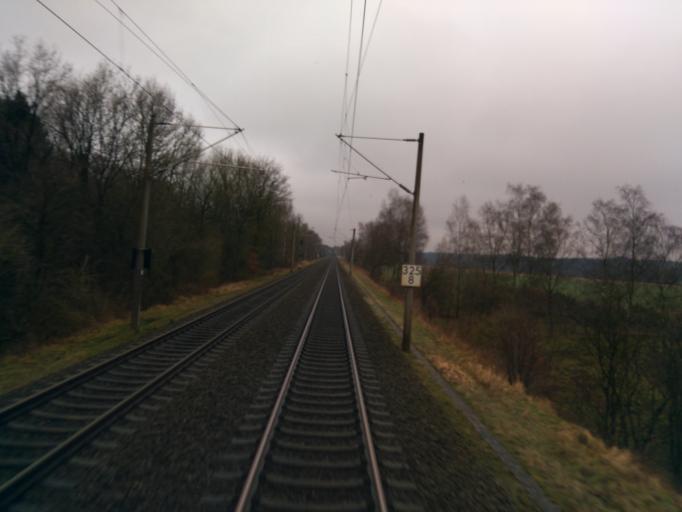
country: DE
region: Lower Saxony
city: Buchholz in der Nordheide
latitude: 53.3410
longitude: 9.9031
